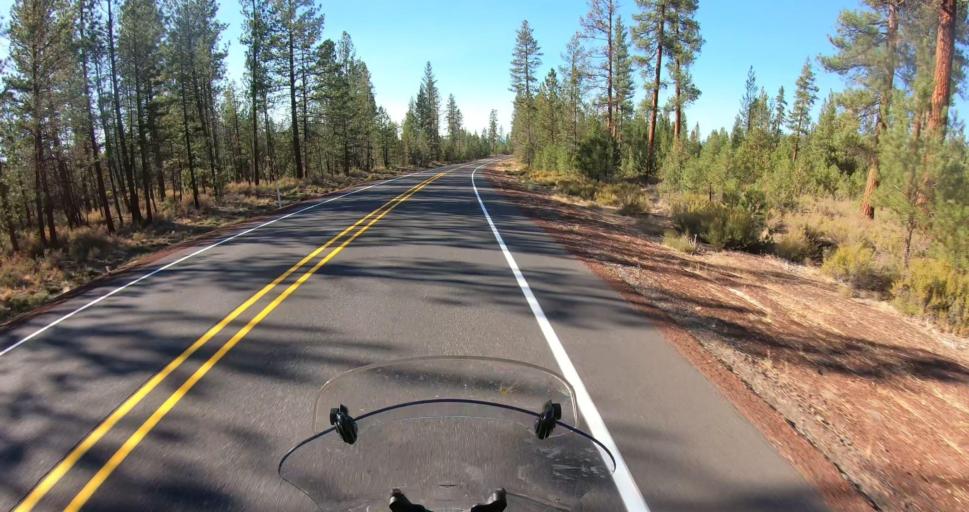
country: US
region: Oregon
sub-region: Deschutes County
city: La Pine
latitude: 43.4930
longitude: -121.4426
